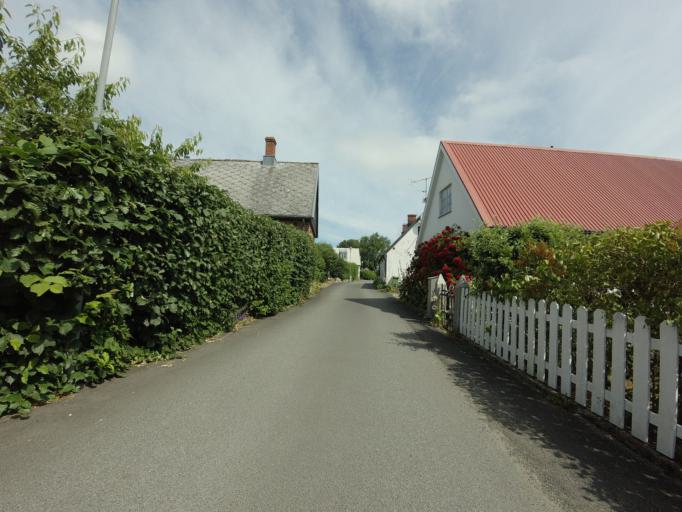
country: SE
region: Skane
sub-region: Simrishamns Kommun
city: Simrishamn
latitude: 55.5193
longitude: 14.3465
